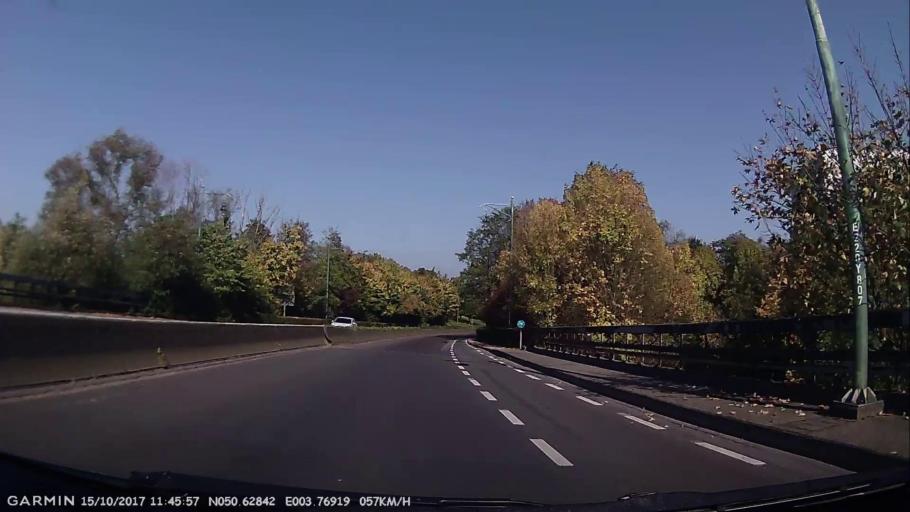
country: BE
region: Wallonia
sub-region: Province du Hainaut
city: Ath
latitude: 50.6285
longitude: 3.7691
